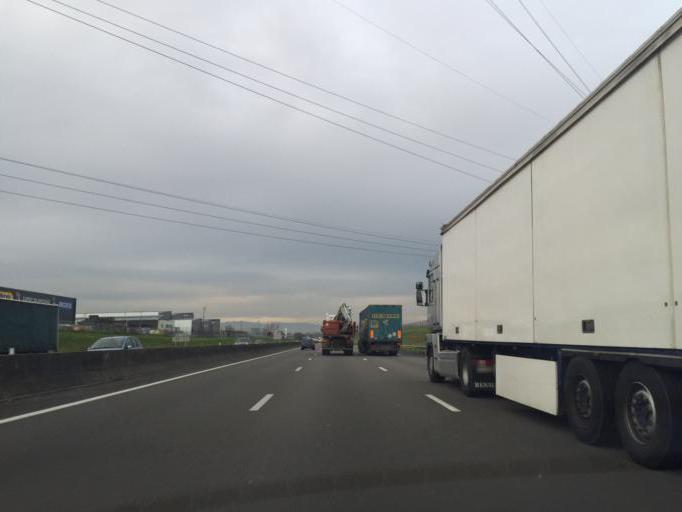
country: FR
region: Rhone-Alpes
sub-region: Departement du Rhone
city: Arnas
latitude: 46.0124
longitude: 4.7293
